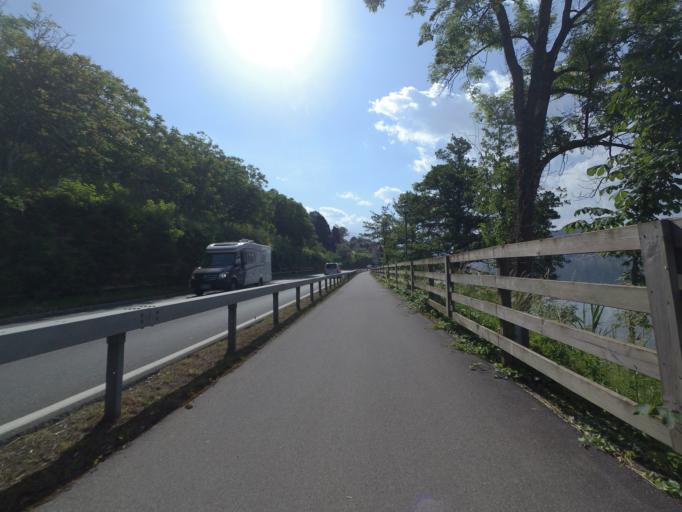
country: AT
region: Carinthia
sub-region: Politischer Bezirk Spittal an der Drau
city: Millstatt
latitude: 46.8077
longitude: 13.5615
